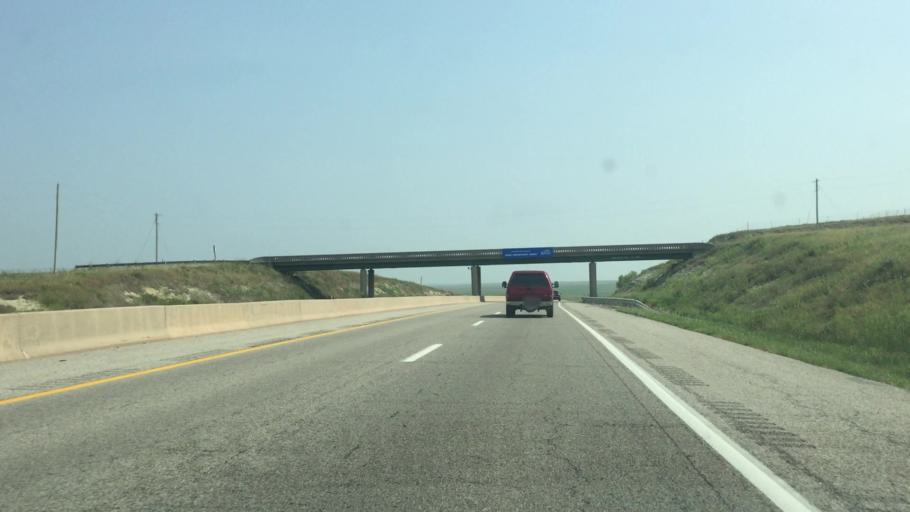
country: US
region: Kansas
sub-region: Chase County
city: Cottonwood Falls
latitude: 38.2750
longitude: -96.3738
